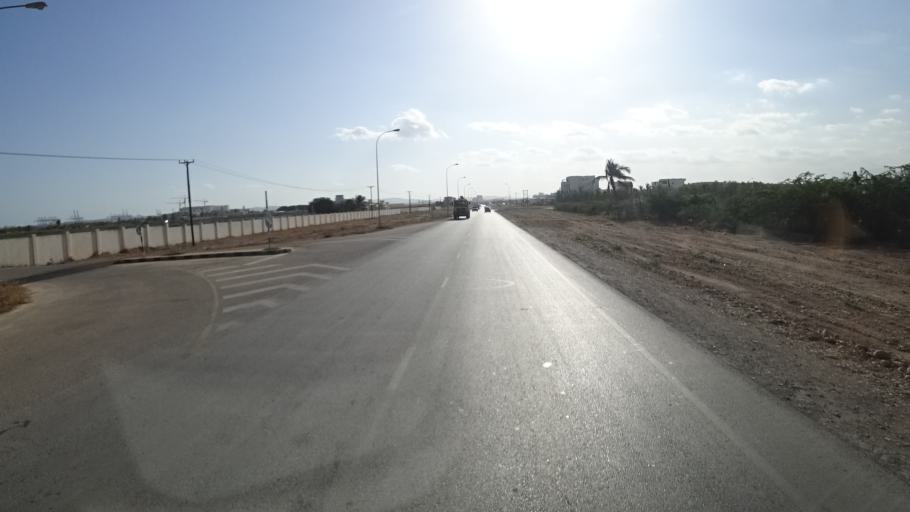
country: OM
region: Zufar
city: Salalah
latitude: 16.9943
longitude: 54.0226
